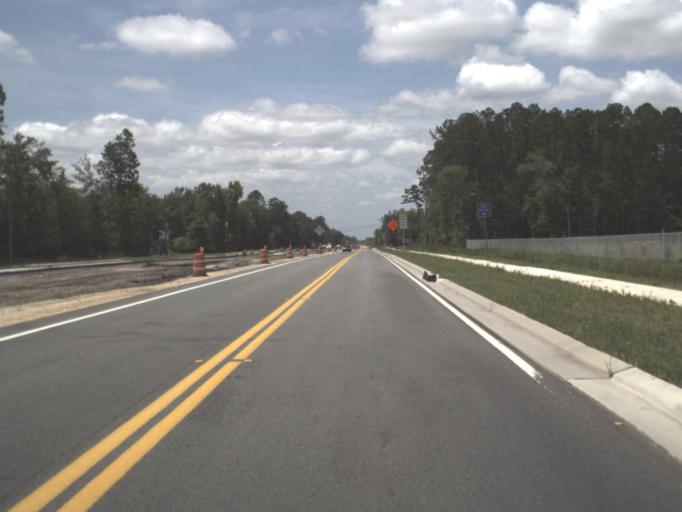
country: US
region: Florida
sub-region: Duval County
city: Baldwin
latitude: 30.3887
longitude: -81.9373
